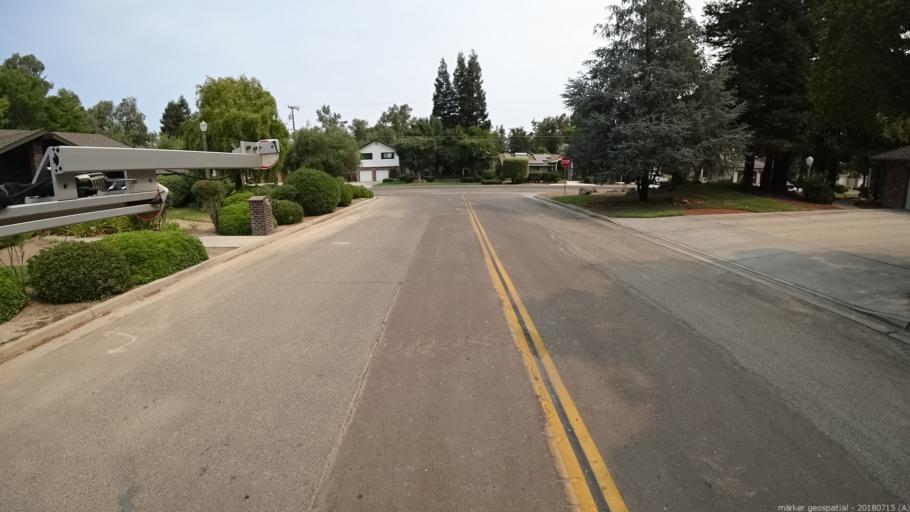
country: US
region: California
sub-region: Madera County
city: Madera Acres
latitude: 37.0243
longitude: -120.0677
